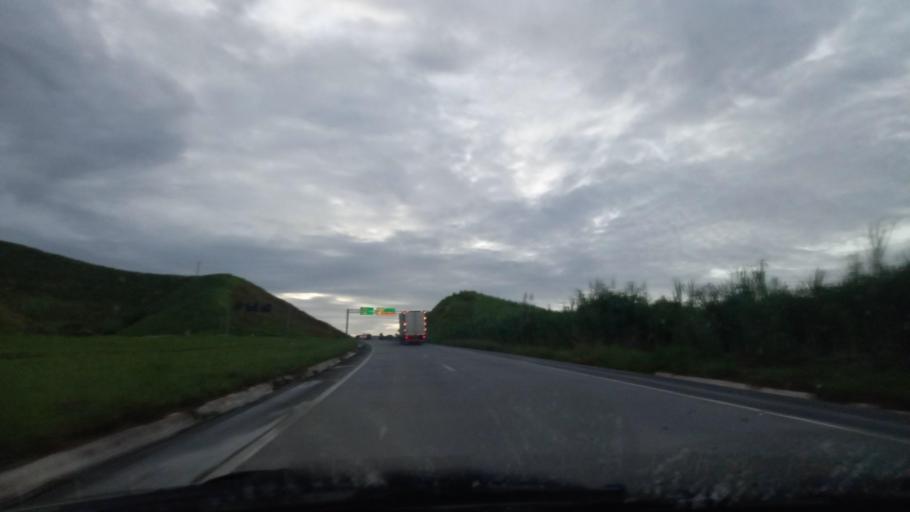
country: BR
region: Pernambuco
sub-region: Ribeirao
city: Ribeirao
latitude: -8.5070
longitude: -35.3869
